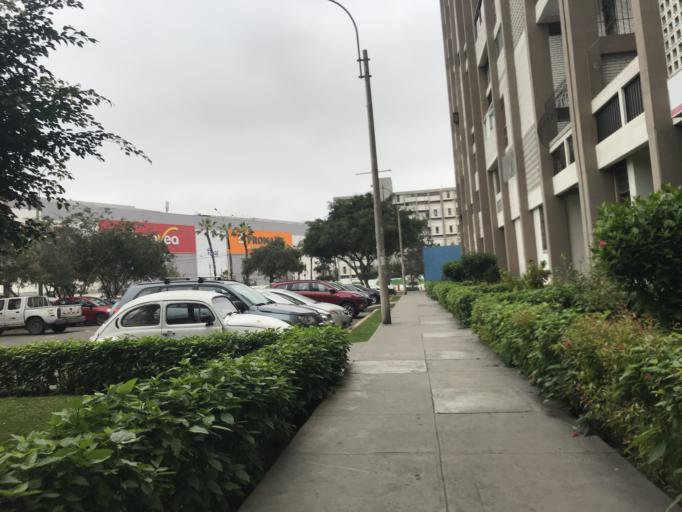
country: PE
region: Lima
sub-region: Lima
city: San Isidro
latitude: -12.0876
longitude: -77.0523
